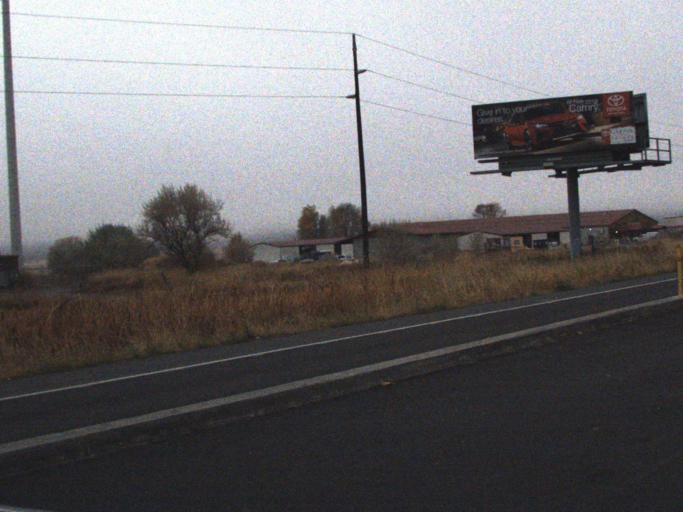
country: US
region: Washington
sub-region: Stevens County
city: Colville
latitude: 48.5531
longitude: -117.9178
